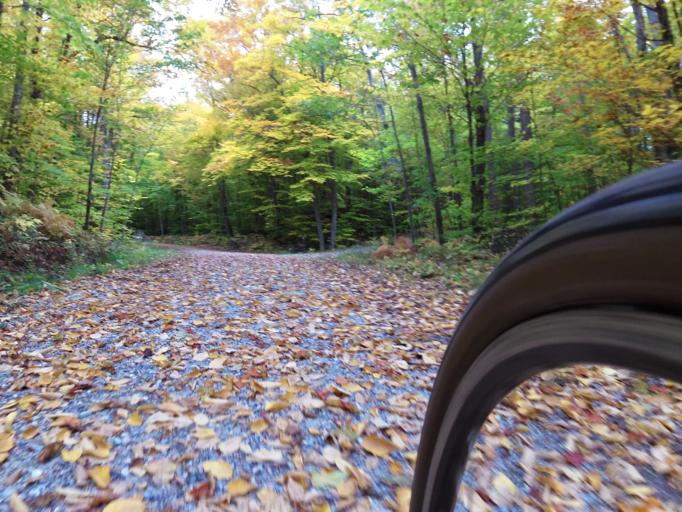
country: CA
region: Quebec
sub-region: Outaouais
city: Wakefield
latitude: 45.6014
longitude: -76.0512
